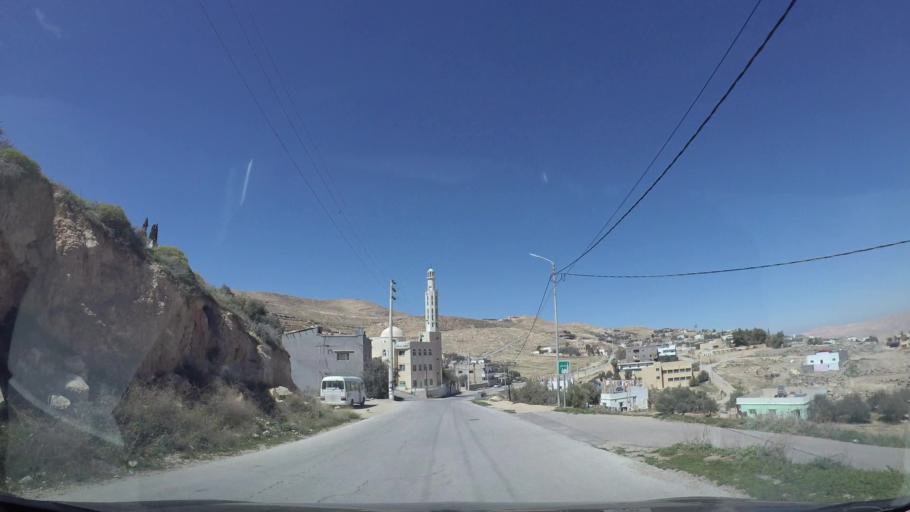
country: JO
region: Tafielah
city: At Tafilah
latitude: 30.8302
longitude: 35.5789
